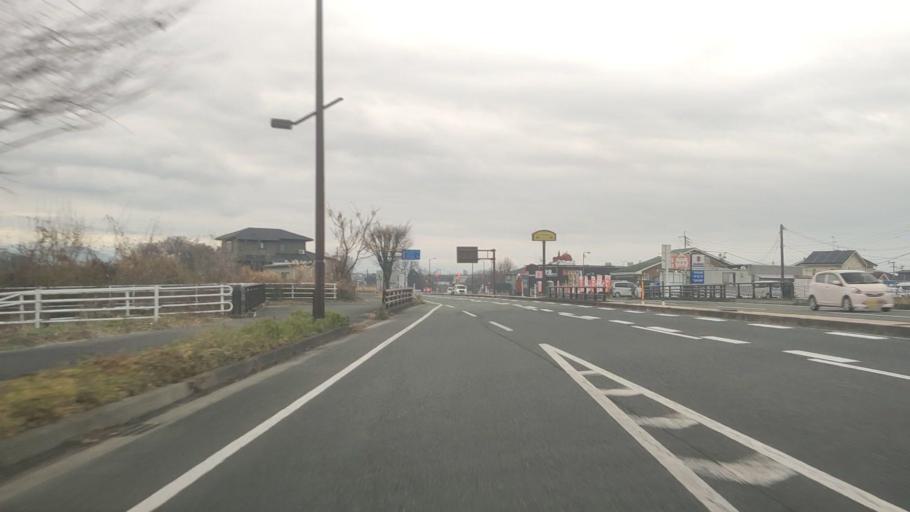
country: JP
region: Kumamoto
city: Ozu
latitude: 32.8239
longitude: 130.7911
